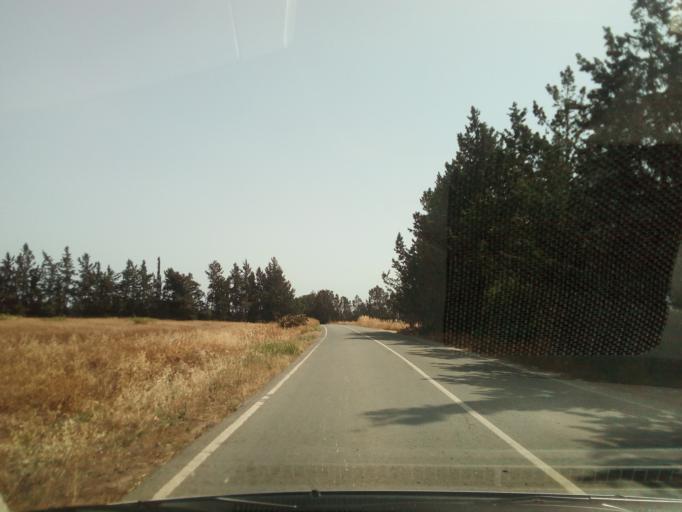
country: CY
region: Larnaka
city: Meneou
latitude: 34.8572
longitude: 33.5954
